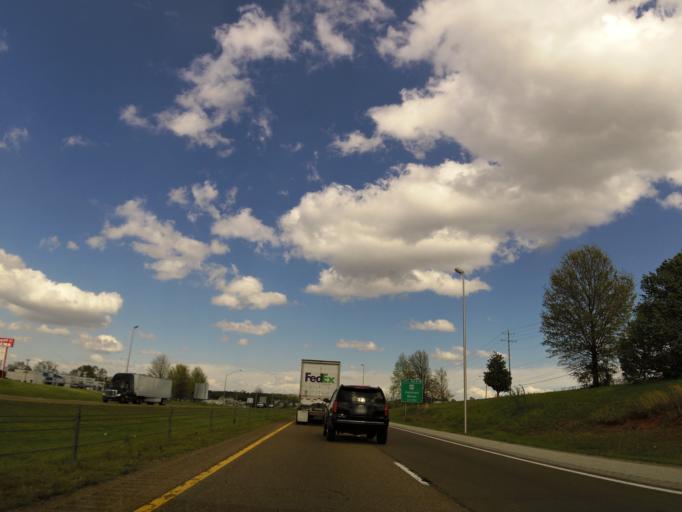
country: US
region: Tennessee
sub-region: Madison County
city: Jackson
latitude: 35.6661
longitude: -88.8464
